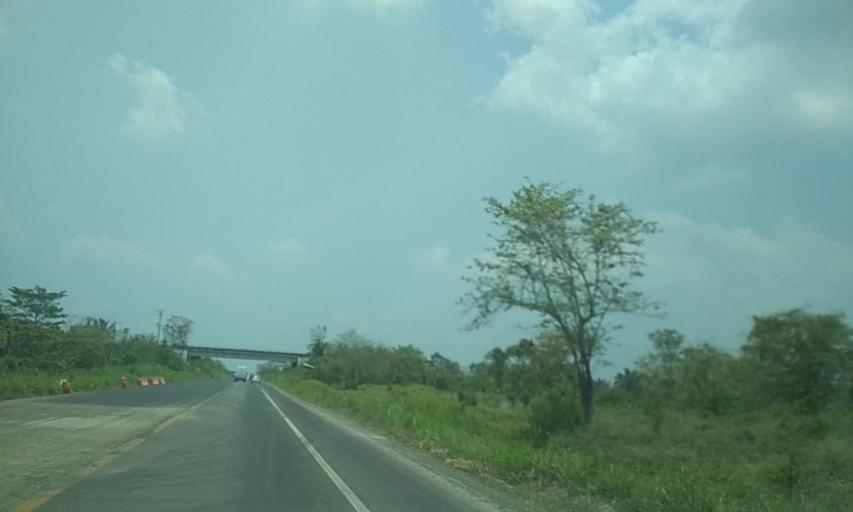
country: MX
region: Tabasco
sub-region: Huimanguillo
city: Francisco Rueda
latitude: 17.6982
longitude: -93.9234
